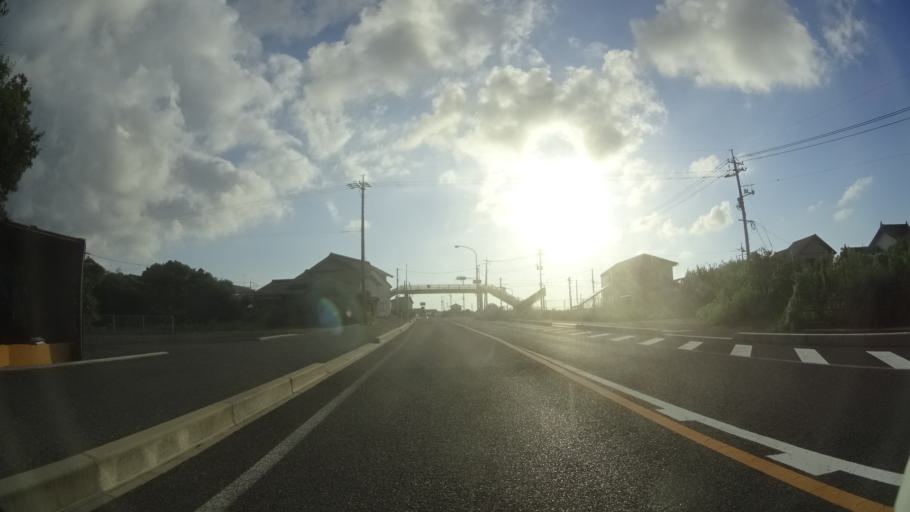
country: JP
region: Tottori
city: Yonago
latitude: 35.5218
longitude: 133.5702
